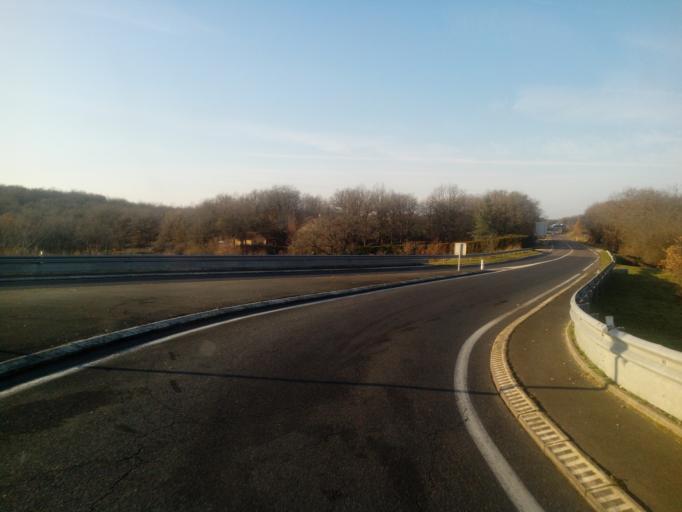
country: FR
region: Midi-Pyrenees
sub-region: Departement du Lot
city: Souillac
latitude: 44.9949
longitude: 1.5362
